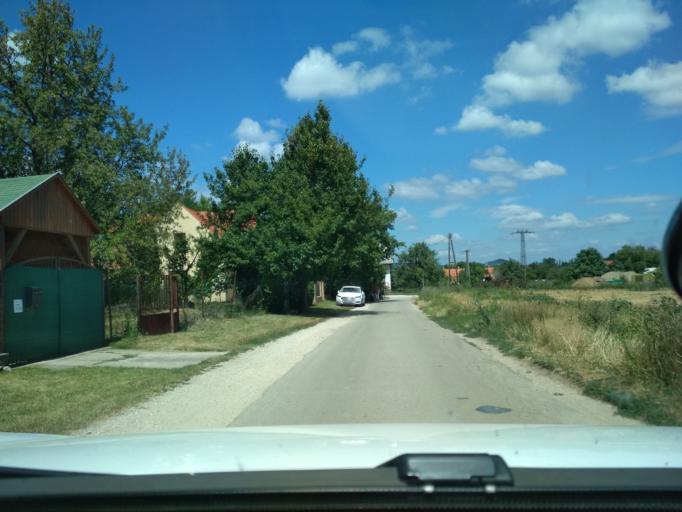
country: HU
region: Fejer
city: Velence
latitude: 47.2161
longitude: 18.6611
